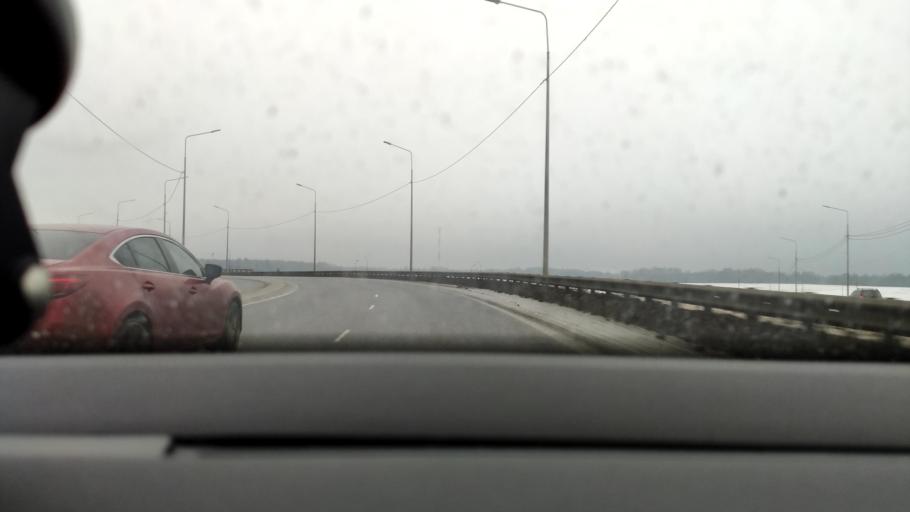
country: RU
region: Moskovskaya
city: Sergiyev Posad
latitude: 56.2757
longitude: 38.1200
